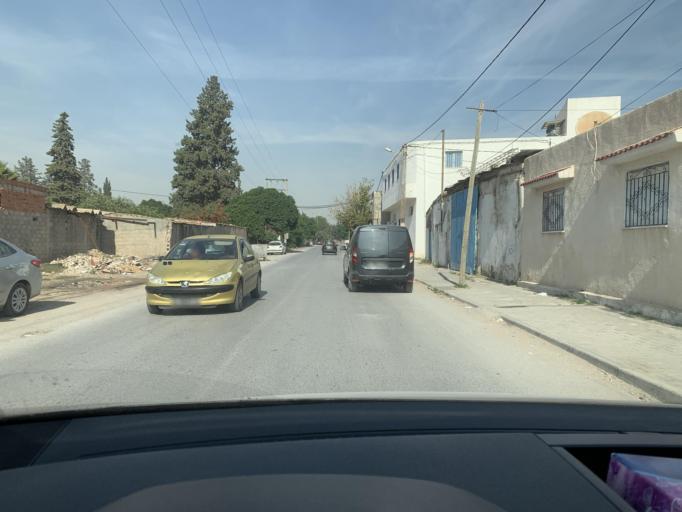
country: TN
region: Manouba
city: Manouba
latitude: 36.8135
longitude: 10.1171
